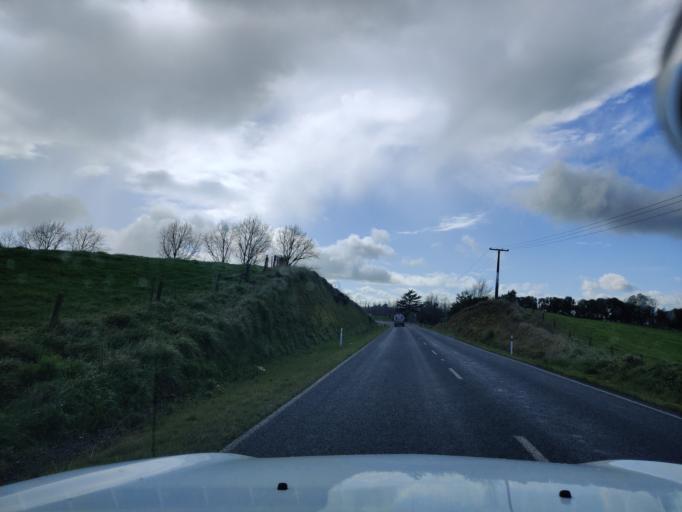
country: NZ
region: Waikato
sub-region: Waikato District
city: Ngaruawahia
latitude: -37.5718
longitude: 175.2508
